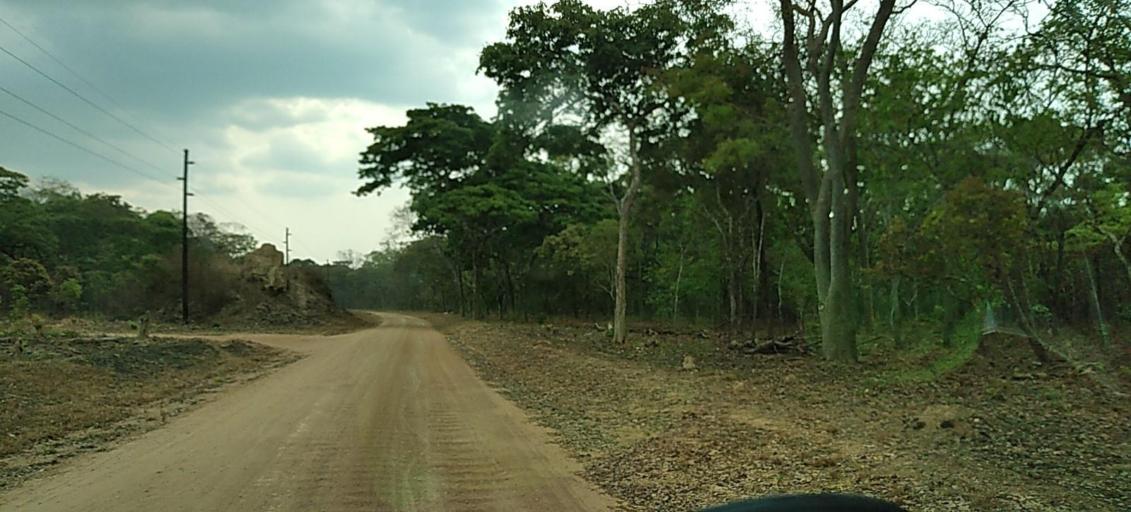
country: ZM
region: North-Western
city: Solwezi
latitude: -12.7767
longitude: 26.4738
